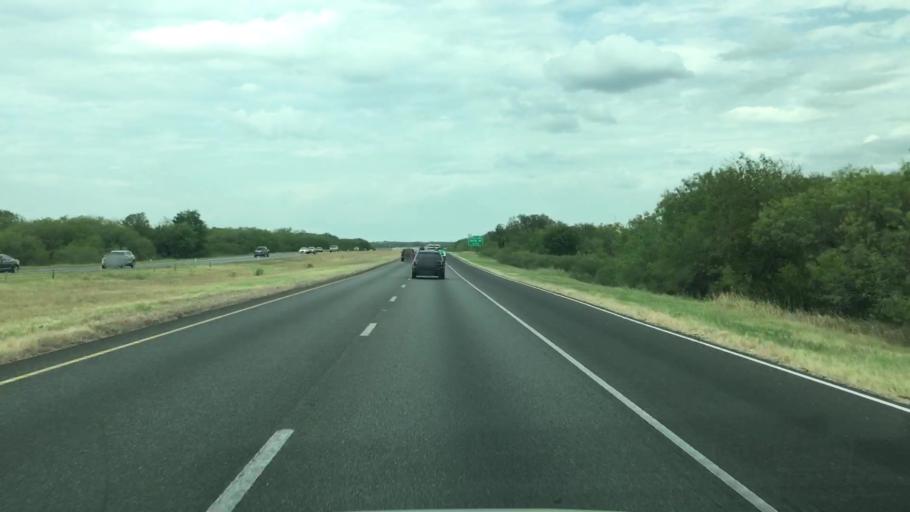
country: US
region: Texas
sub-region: Bexar County
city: Elmendorf
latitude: 29.1295
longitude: -98.4301
